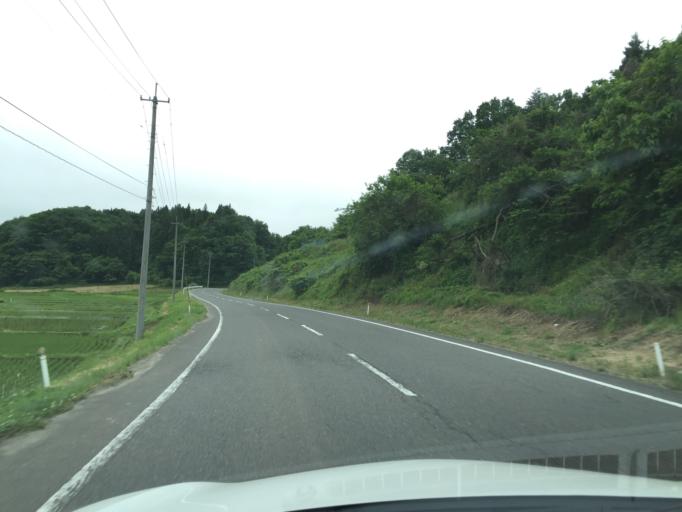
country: JP
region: Fukushima
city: Funehikimachi-funehiki
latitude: 37.3175
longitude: 140.6298
